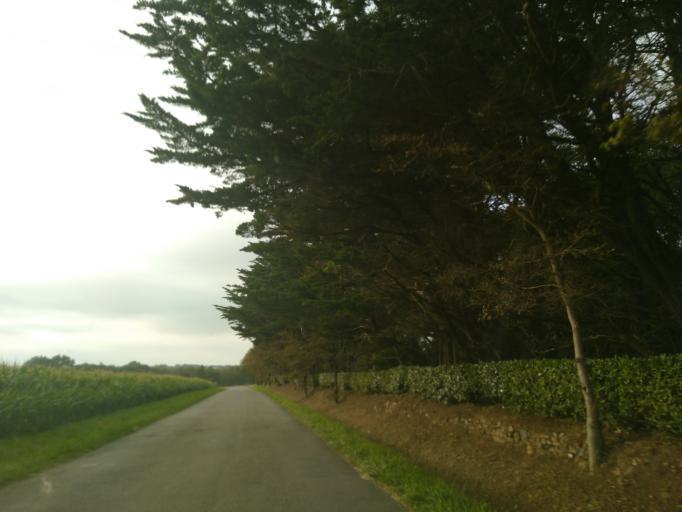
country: FR
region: Brittany
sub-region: Departement du Finistere
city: Crozon
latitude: 48.2387
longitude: -4.4468
